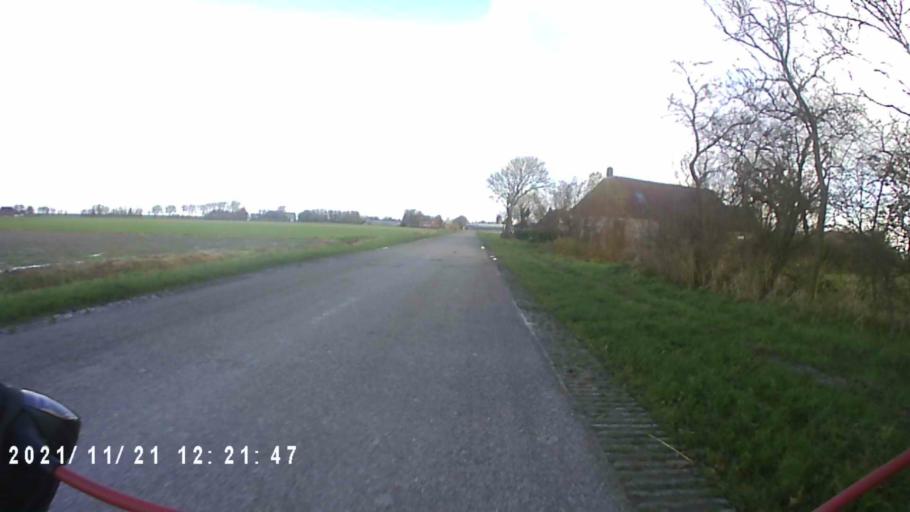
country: NL
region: Friesland
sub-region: Gemeente Dongeradeel
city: Ternaard
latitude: 53.3926
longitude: 6.0386
